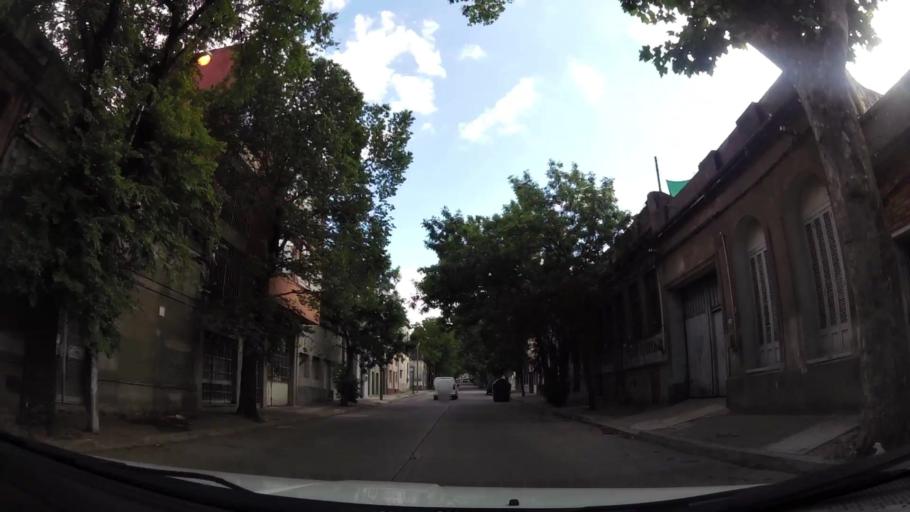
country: UY
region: Montevideo
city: Montevideo
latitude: -34.8808
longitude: -56.1807
